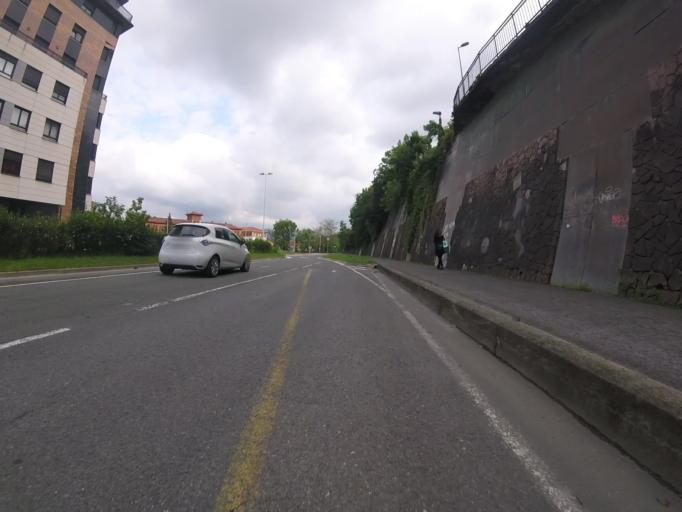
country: ES
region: Basque Country
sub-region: Provincia de Guipuzcoa
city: San Sebastian
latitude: 43.3082
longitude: -1.9668
